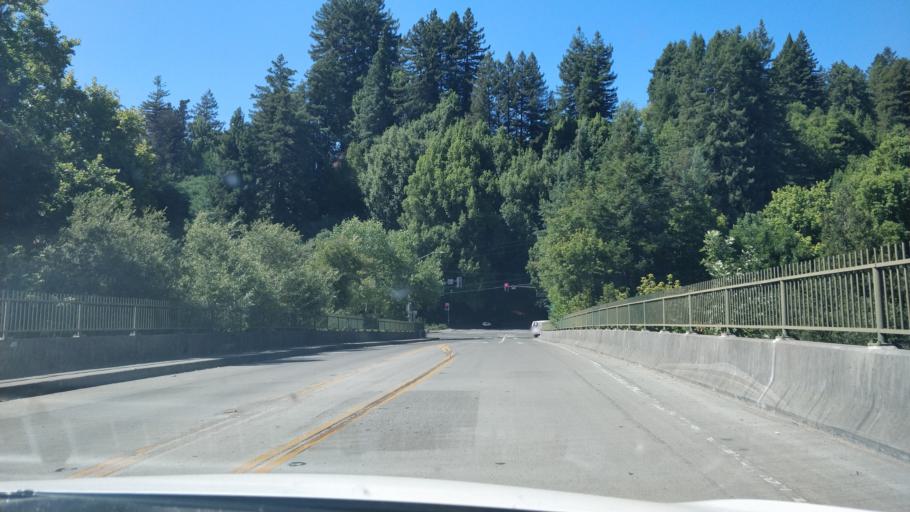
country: US
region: California
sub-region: Sonoma County
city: Guerneville
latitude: 38.5017
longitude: -122.9948
